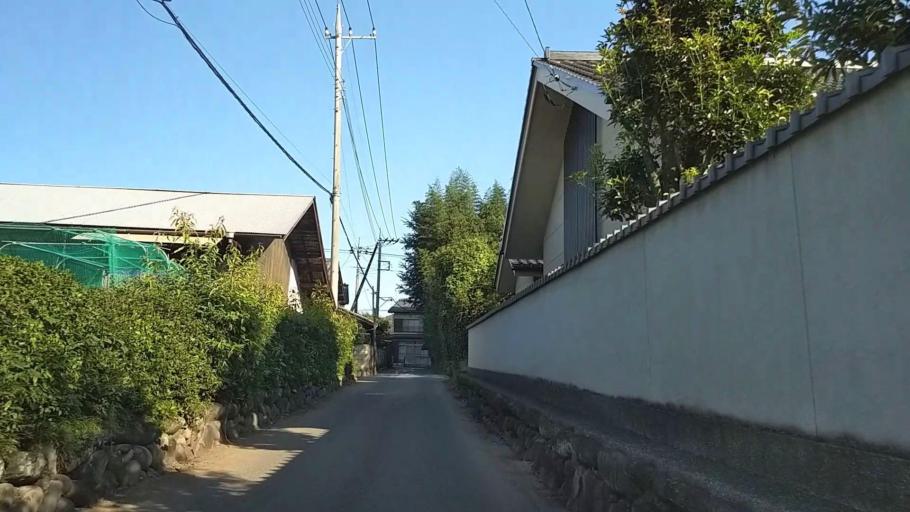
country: JP
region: Gunma
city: Annaka
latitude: 36.3305
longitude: 138.8978
